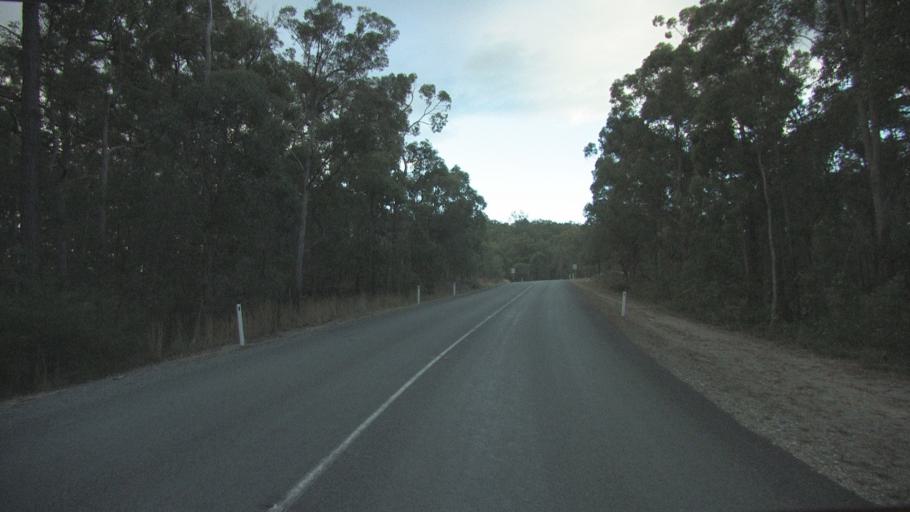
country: AU
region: Queensland
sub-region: Logan
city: Chambers Flat
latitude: -27.8031
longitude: 153.1437
